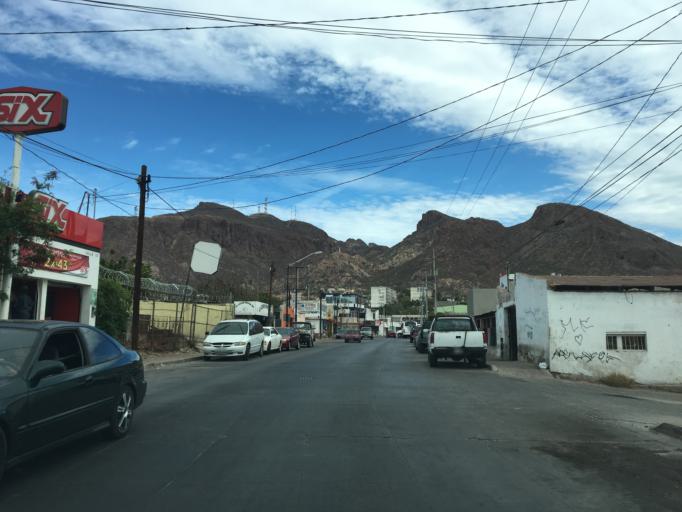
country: MX
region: Sonora
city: Heroica Guaymas
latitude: 27.9211
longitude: -110.9027
